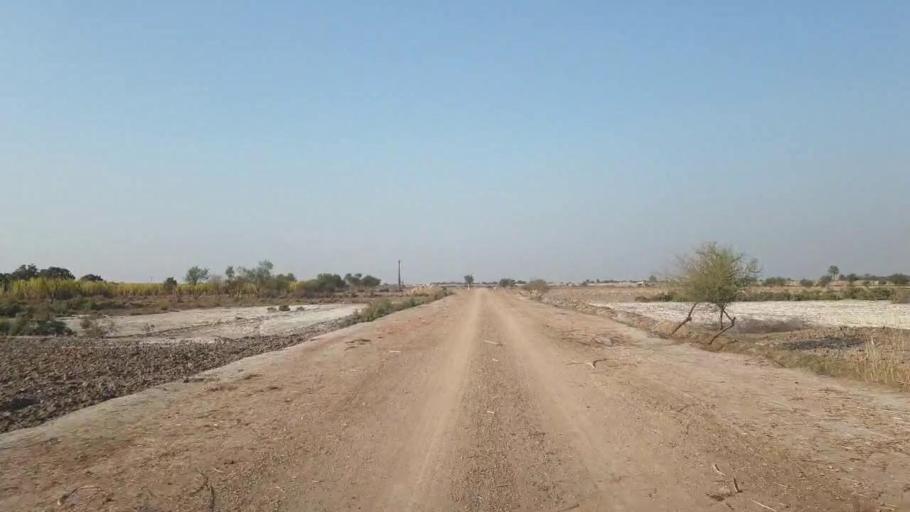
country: PK
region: Sindh
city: Mirpur Khas
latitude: 25.4518
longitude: 68.9334
